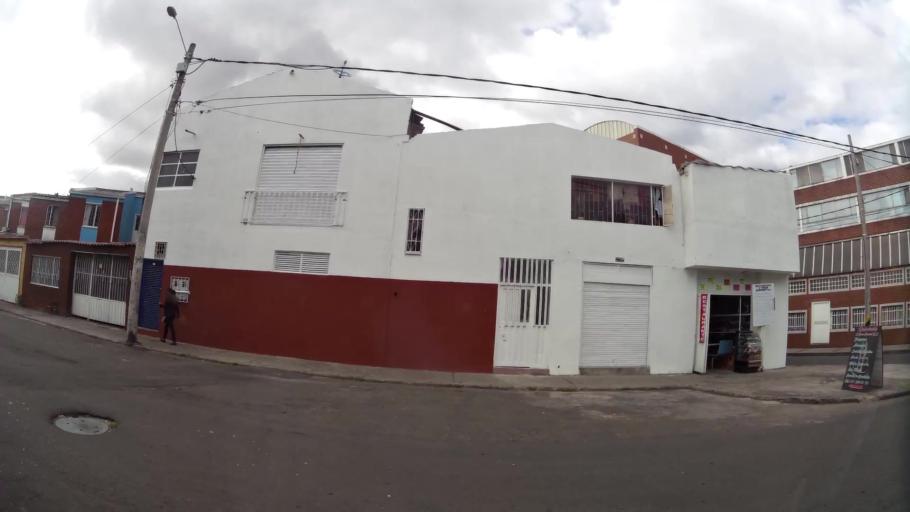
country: CO
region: Bogota D.C.
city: Bogota
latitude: 4.6078
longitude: -74.1358
